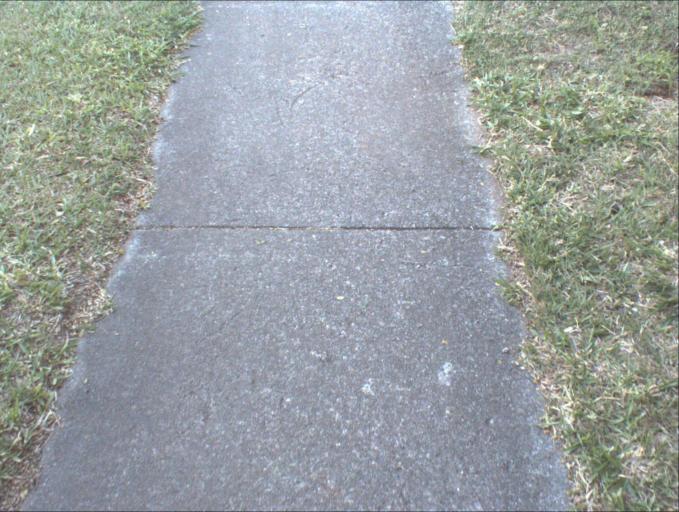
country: AU
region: Queensland
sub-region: Logan
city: Beenleigh
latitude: -27.6732
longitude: 153.2041
